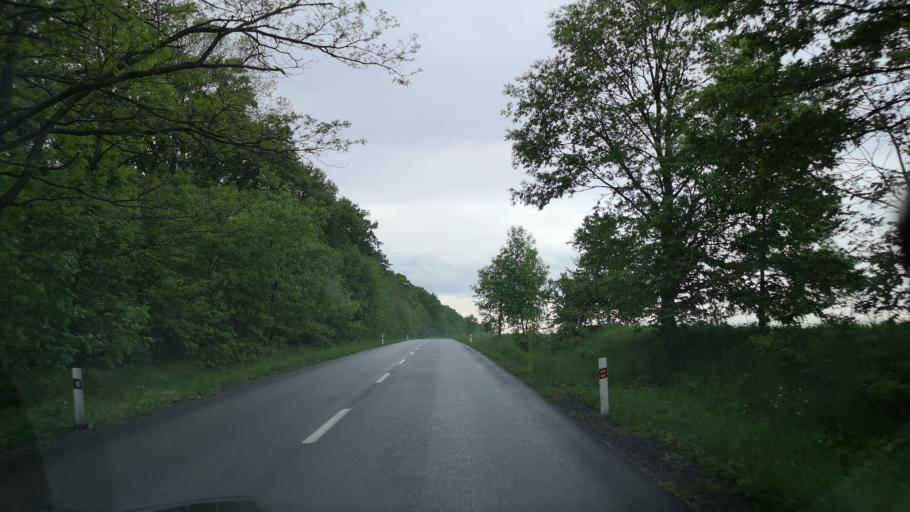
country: SK
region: Nitriansky
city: Sellye
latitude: 48.2196
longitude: 17.9843
